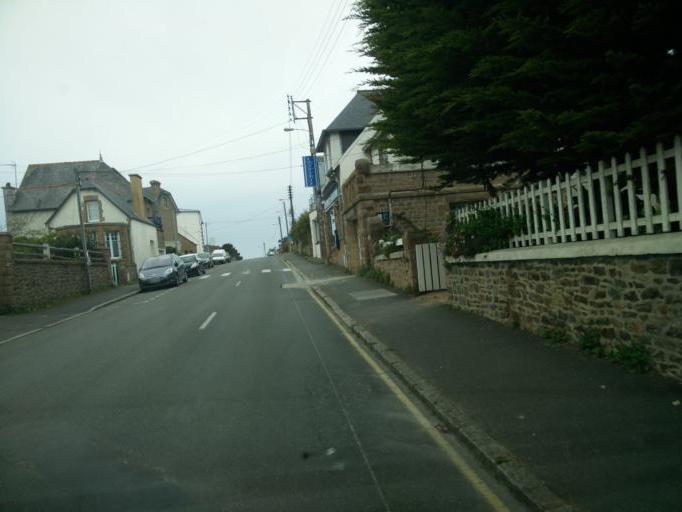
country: FR
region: Brittany
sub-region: Departement des Cotes-d'Armor
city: Tregastel
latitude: 48.8275
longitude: -3.5145
